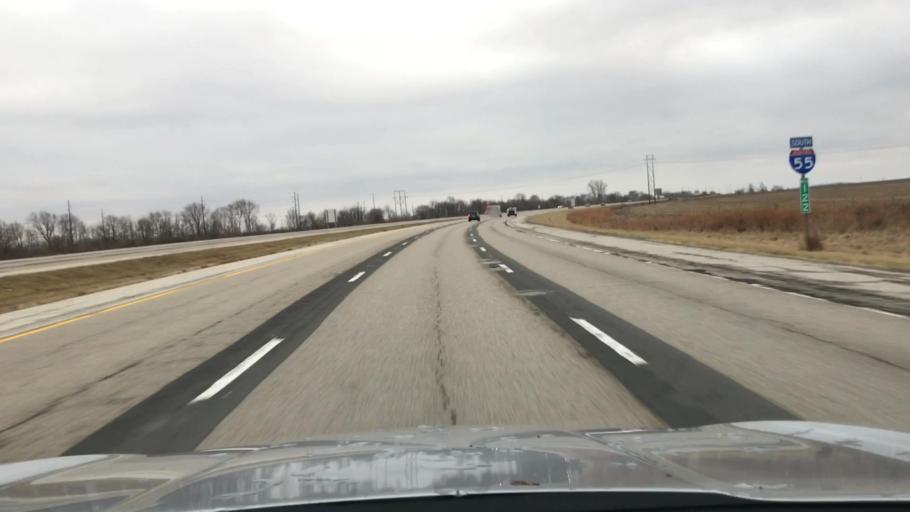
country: US
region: Illinois
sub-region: Logan County
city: Lincoln
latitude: 40.1039
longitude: -89.4165
